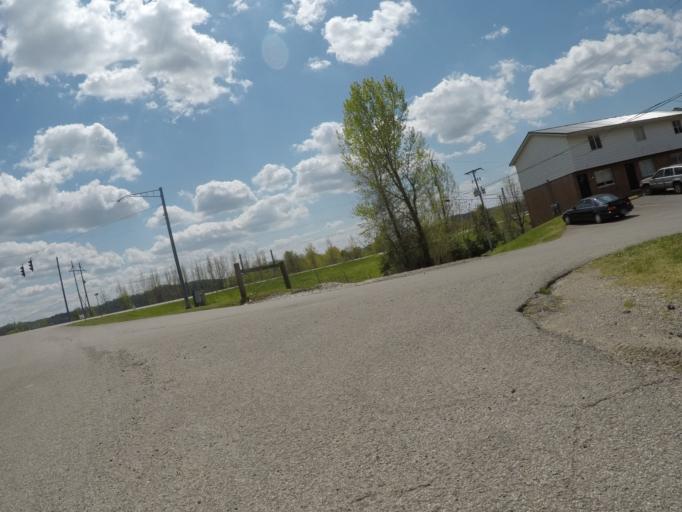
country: US
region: West Virginia
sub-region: Cabell County
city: Huntington
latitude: 38.4455
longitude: -82.3815
